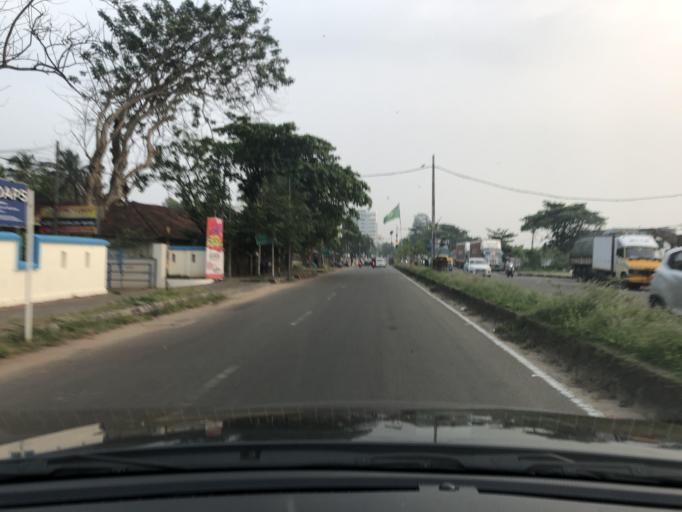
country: IN
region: Kerala
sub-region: Kozhikode
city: Kozhikode
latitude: 11.2645
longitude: 75.7676
